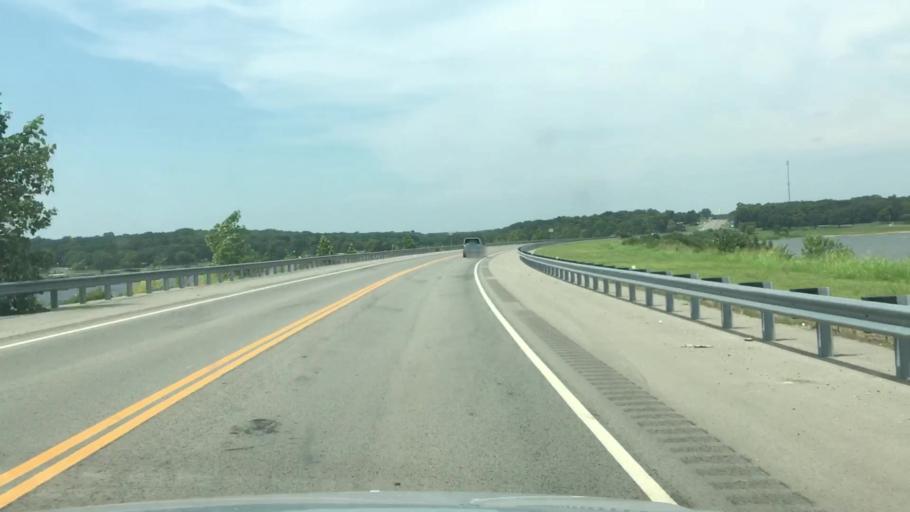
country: US
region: Oklahoma
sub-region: Wagoner County
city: Wagoner
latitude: 35.9310
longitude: -95.2731
